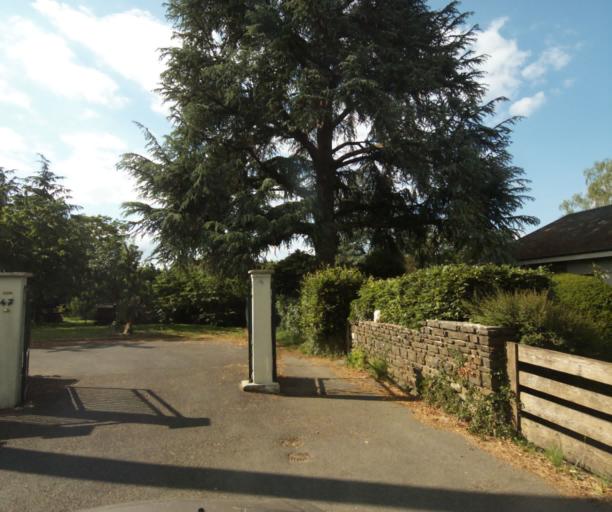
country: FR
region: Champagne-Ardenne
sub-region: Departement des Ardennes
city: Montcy-Notre-Dame
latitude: 49.7794
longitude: 4.7339
